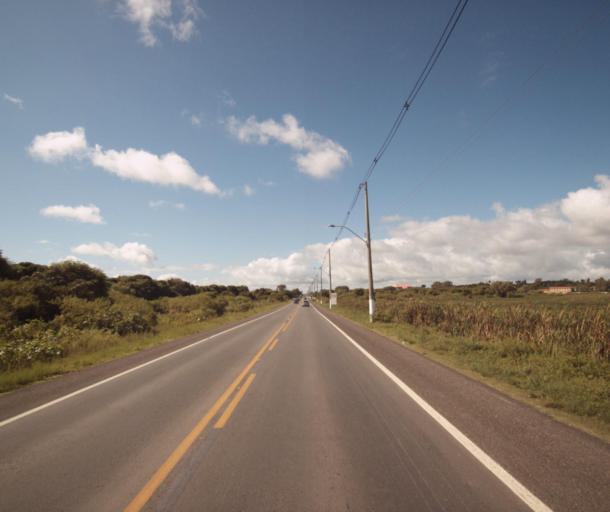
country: BR
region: Rio Grande do Sul
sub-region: Pelotas
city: Pelotas
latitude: -31.7504
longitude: -52.3600
